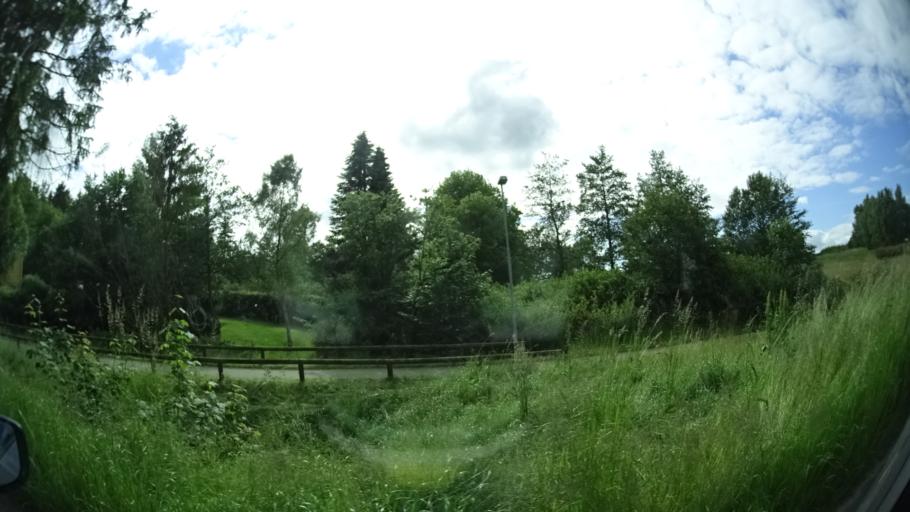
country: DK
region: Central Jutland
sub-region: Norddjurs Kommune
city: Grenaa
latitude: 56.4954
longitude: 10.7387
